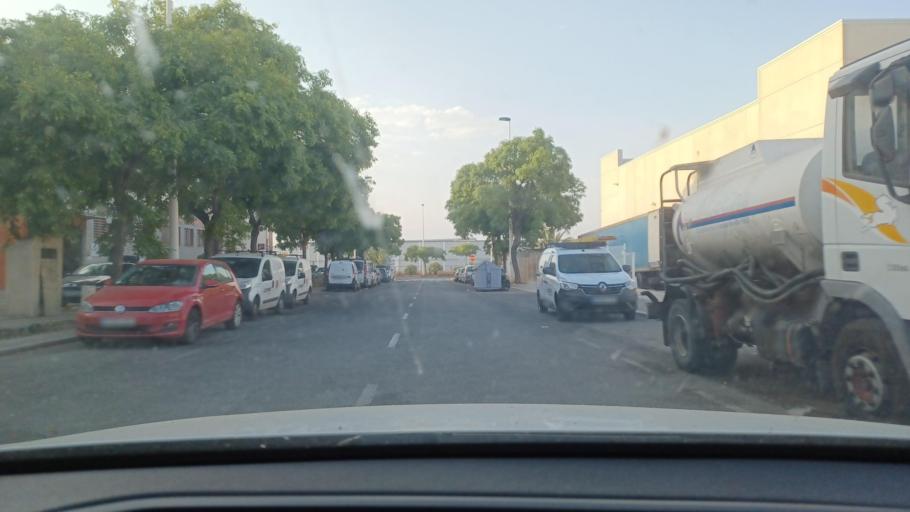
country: ES
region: Valencia
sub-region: Provincia de Alicante
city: Elche
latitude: 38.2933
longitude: -0.6190
